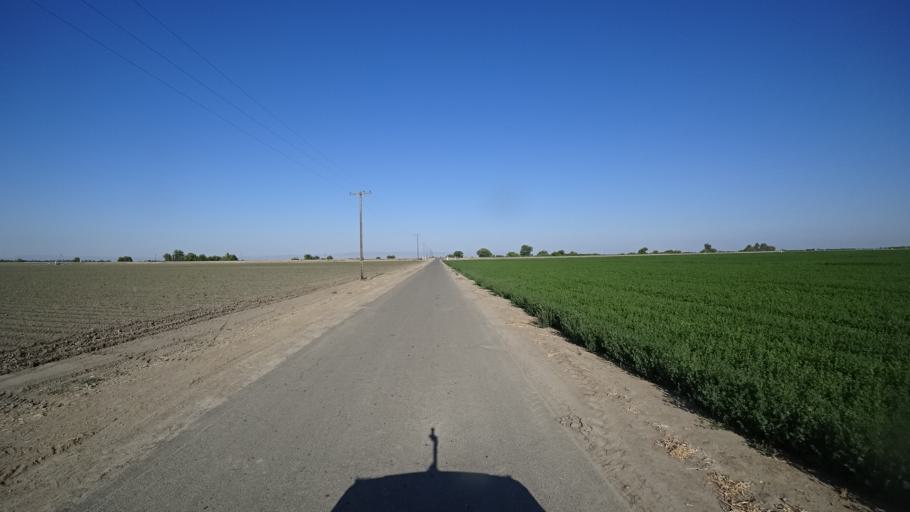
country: US
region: California
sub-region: Fresno County
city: Riverdale
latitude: 36.4015
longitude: -119.9191
